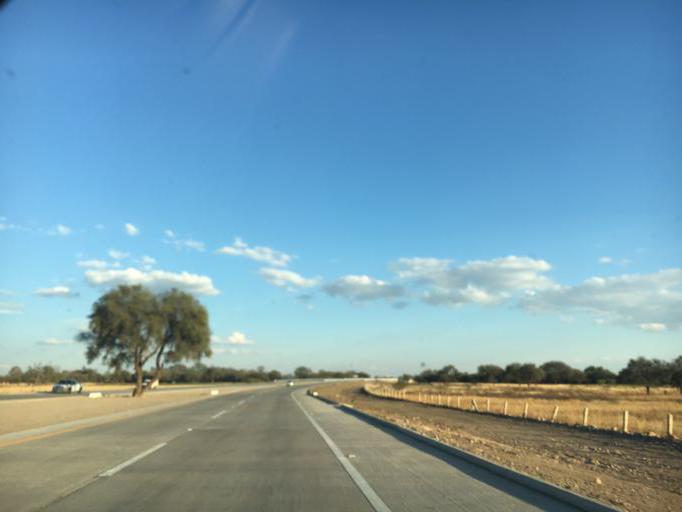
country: MX
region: Guanajuato
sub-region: Leon
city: Ladrilleras del Refugio
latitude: 21.0959
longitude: -101.5664
